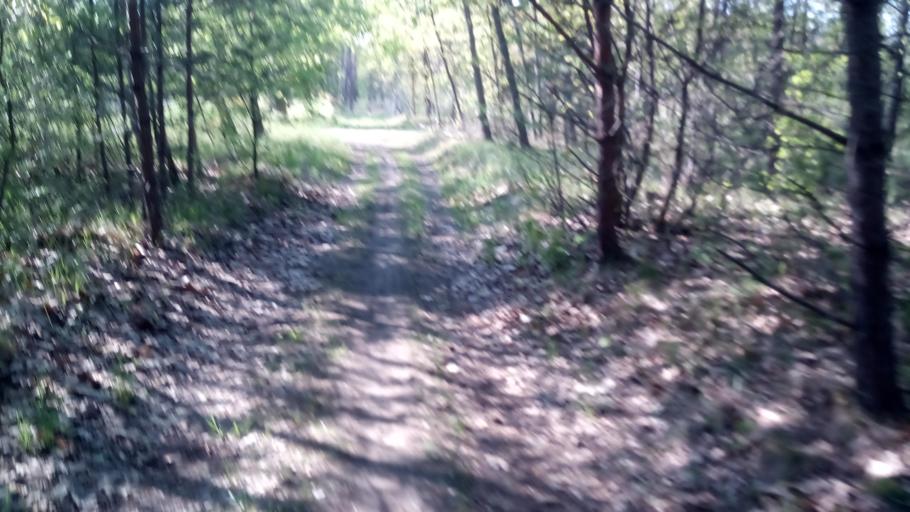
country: PL
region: Opole Voivodeship
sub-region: Powiat opolski
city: Tarnow Opolski
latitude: 50.5883
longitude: 18.0474
